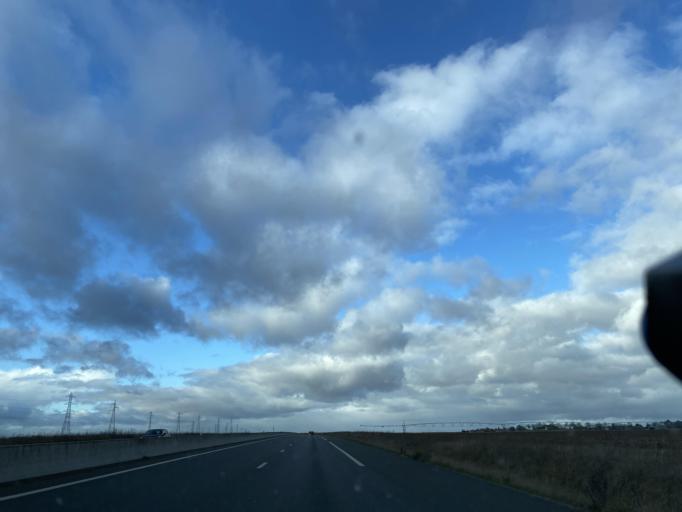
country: FR
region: Centre
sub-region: Departement d'Eure-et-Loir
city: Voves
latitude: 48.3400
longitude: 1.6365
